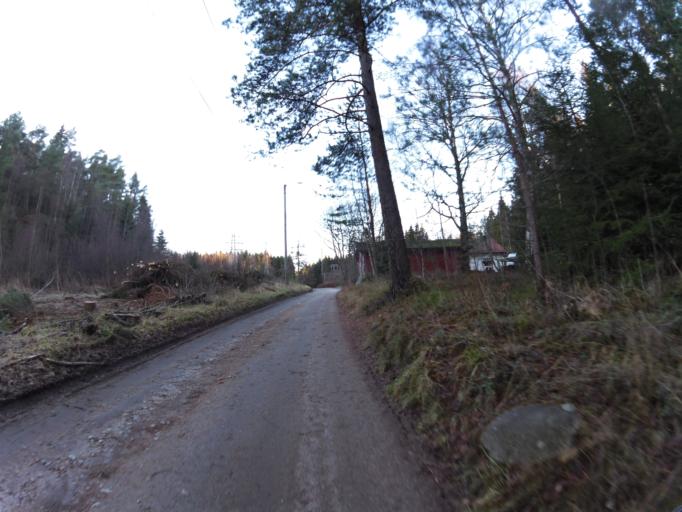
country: NO
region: Ostfold
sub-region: Fredrikstad
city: Fredrikstad
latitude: 59.2442
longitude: 10.9624
